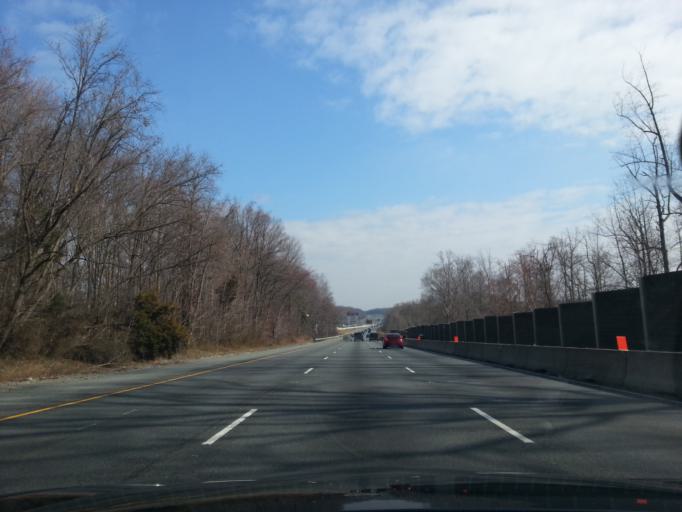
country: US
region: Virginia
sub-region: Stafford County
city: Aquia Harbour
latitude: 38.4762
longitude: -77.3996
